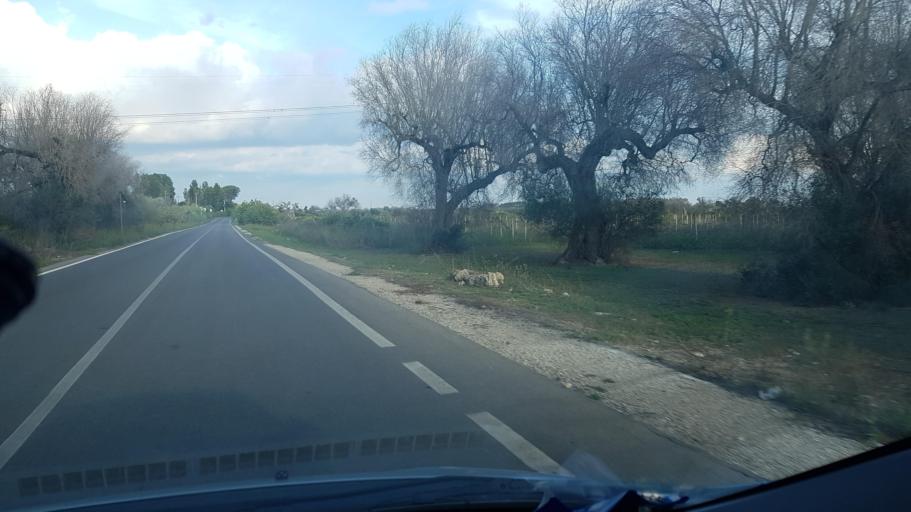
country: IT
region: Apulia
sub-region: Provincia di Lecce
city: Carmiano
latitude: 40.3396
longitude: 18.0033
